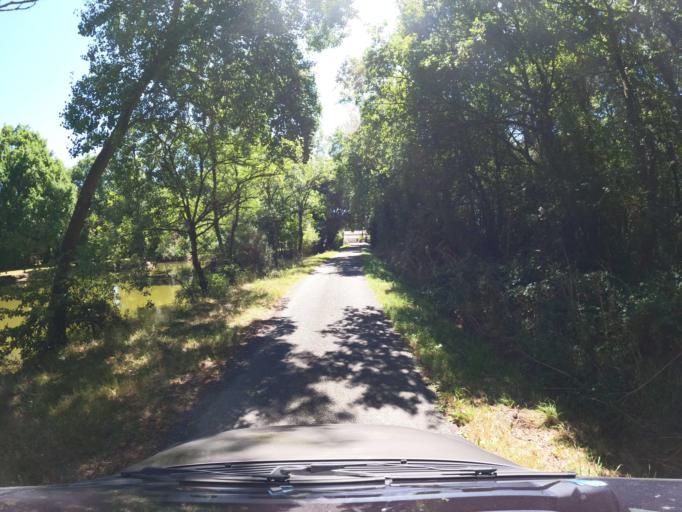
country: FR
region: Pays de la Loire
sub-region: Departement de la Loire-Atlantique
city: La Limouziniere
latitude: 46.9419
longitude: -1.6229
